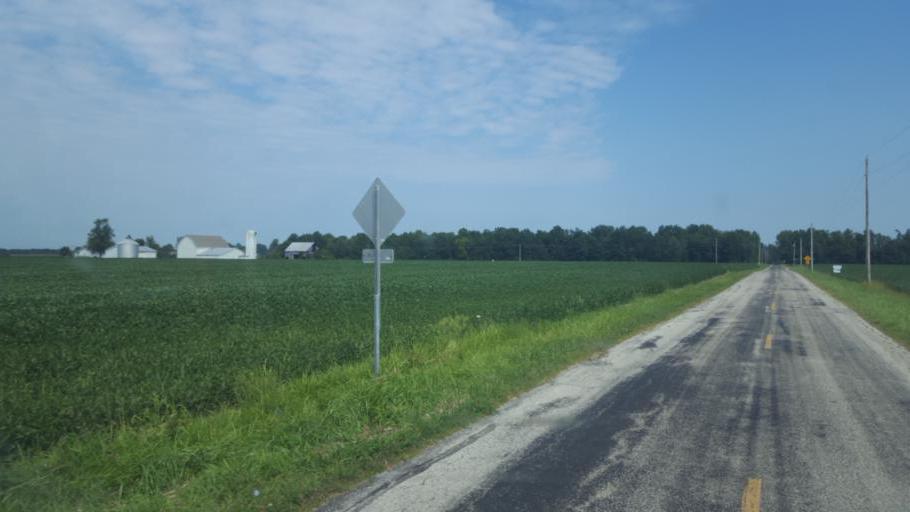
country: US
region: Ohio
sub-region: Delaware County
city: Ashley
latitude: 40.4927
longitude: -83.0053
